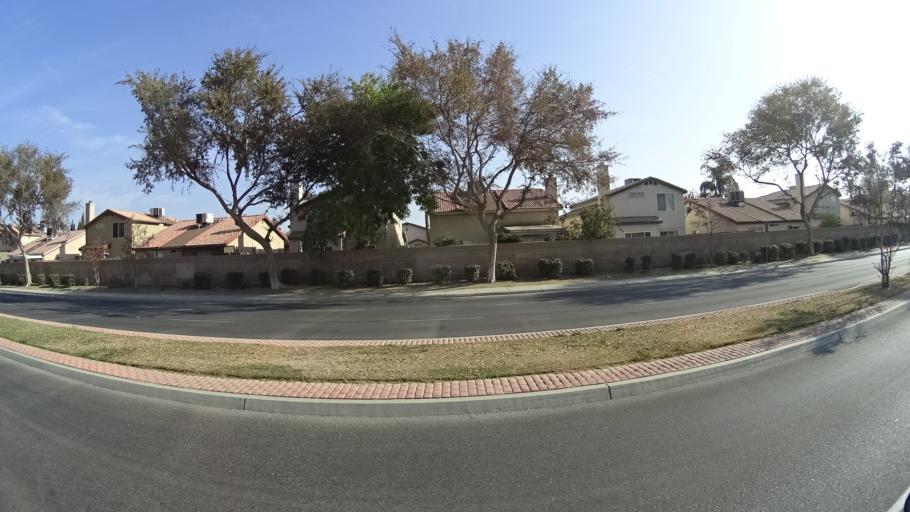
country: US
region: California
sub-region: Kern County
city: Greenacres
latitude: 35.3186
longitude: -119.1093
